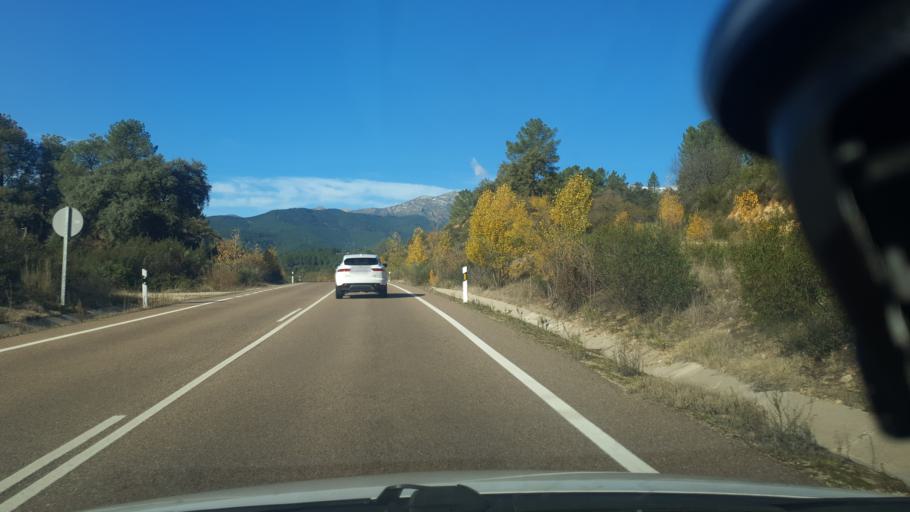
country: ES
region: Castille and Leon
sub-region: Provincia de Avila
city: Arenas de San Pedro
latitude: 40.1896
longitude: -5.0688
